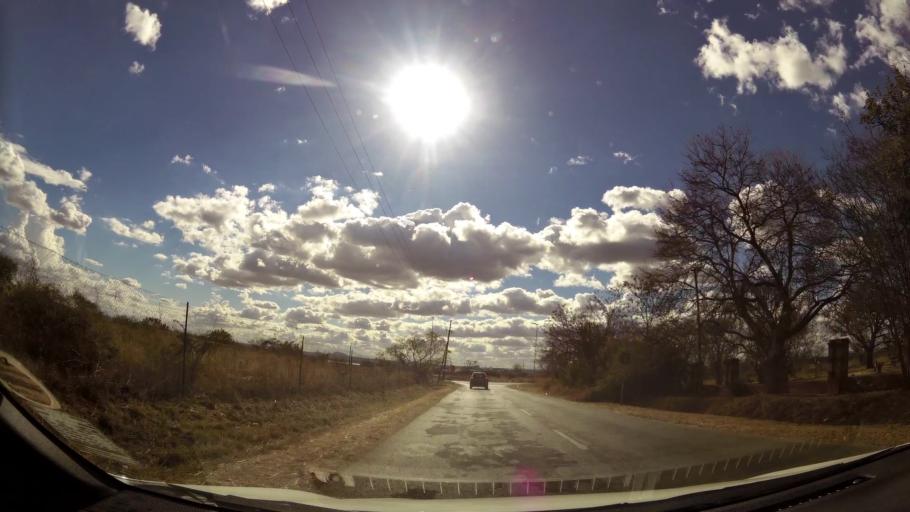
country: ZA
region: Limpopo
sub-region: Capricorn District Municipality
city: Polokwane
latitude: -23.8758
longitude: 29.4794
